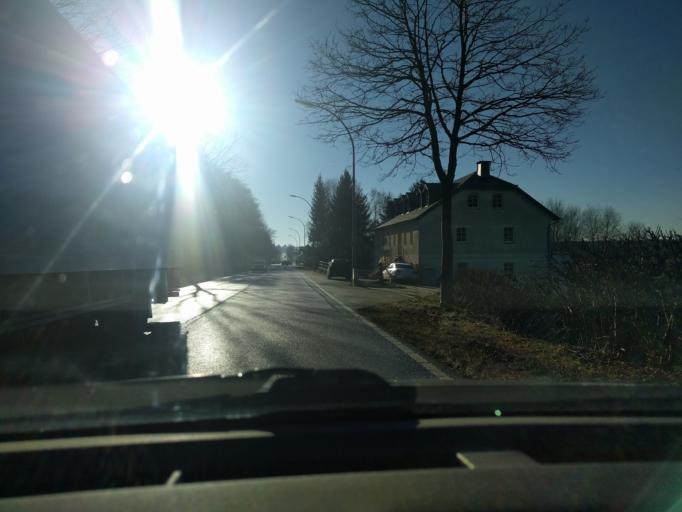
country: LU
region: Diekirch
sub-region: Canton de Clervaux
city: Troisvierges
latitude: 50.1740
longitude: 6.0252
